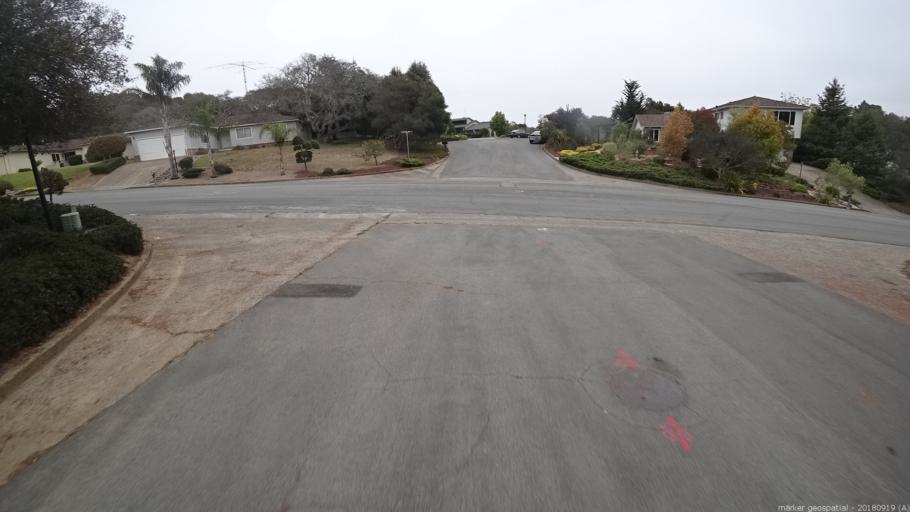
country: US
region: California
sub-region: Monterey County
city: Castroville
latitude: 36.7803
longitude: -121.7176
